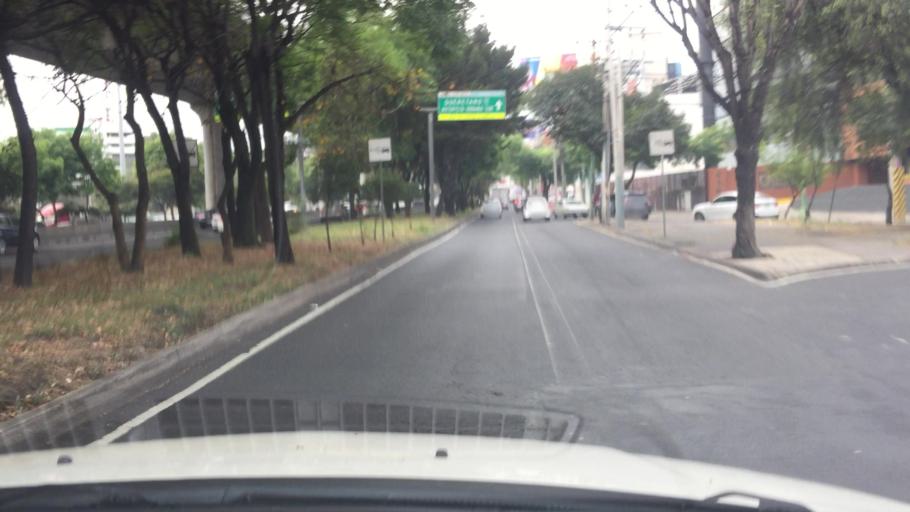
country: MX
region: Mexico City
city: Magdalena Contreras
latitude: 19.3059
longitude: -99.2060
